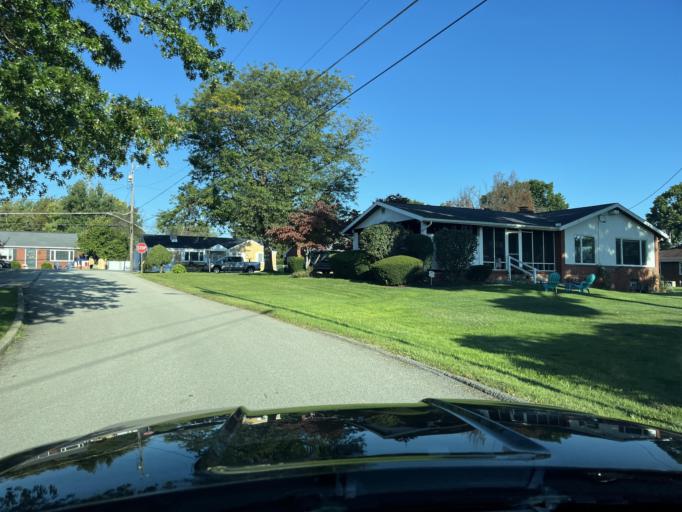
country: US
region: Pennsylvania
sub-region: Fayette County
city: Leith-Hatfield
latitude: 39.8793
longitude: -79.7348
